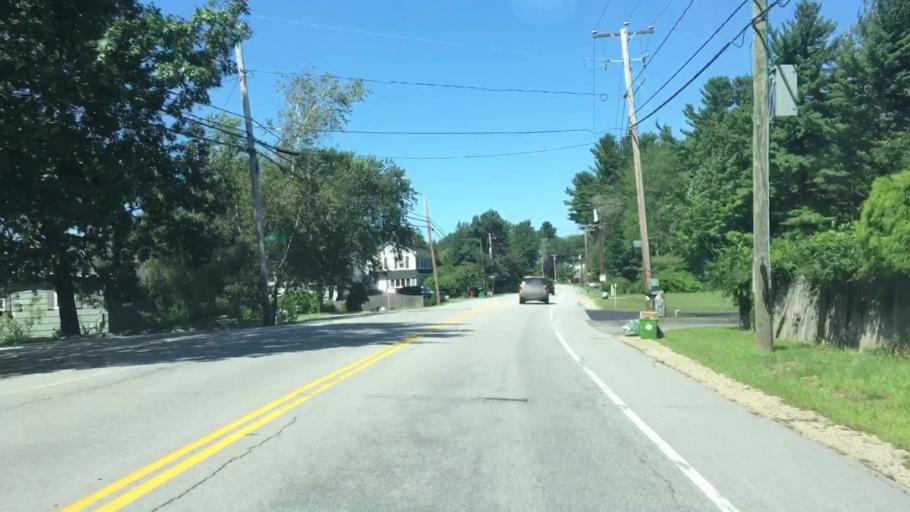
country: US
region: Maine
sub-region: York County
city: Eliot
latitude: 43.1414
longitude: -70.8385
